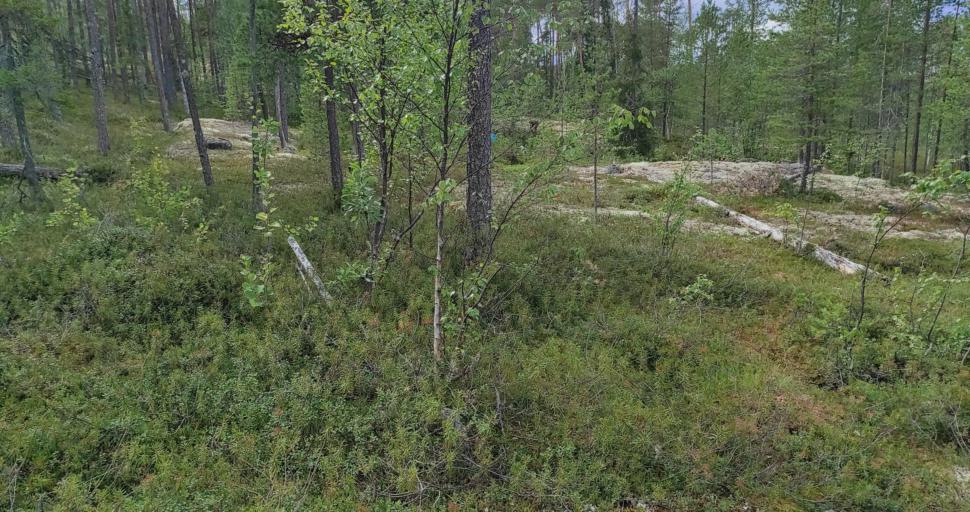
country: RU
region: Murmansk
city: Poyakonda
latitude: 66.7749
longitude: 32.7438
